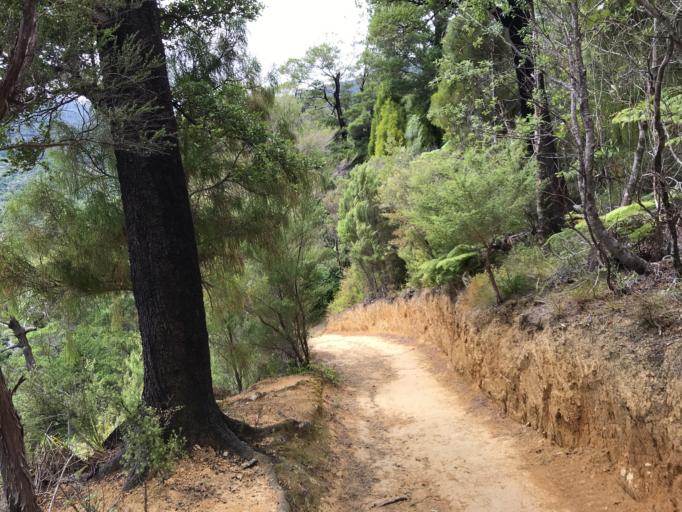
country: NZ
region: Marlborough
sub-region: Marlborough District
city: Picton
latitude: -41.0974
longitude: 174.1875
